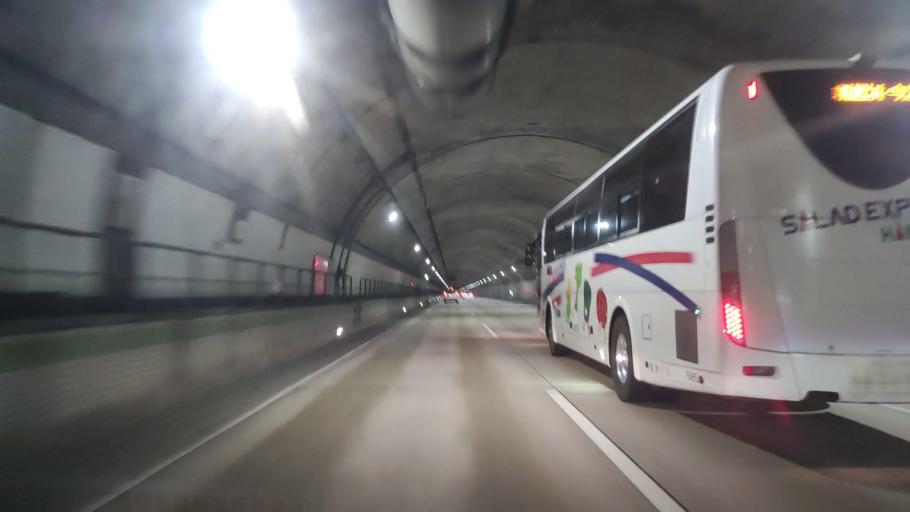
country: JP
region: Hyogo
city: Akashi
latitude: 34.6495
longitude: 135.0572
